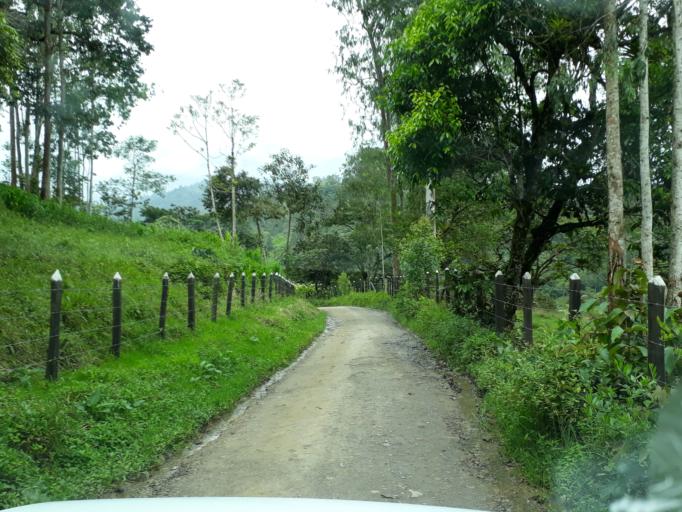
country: CO
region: Cundinamarca
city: Gacheta
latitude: 4.8459
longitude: -73.6482
